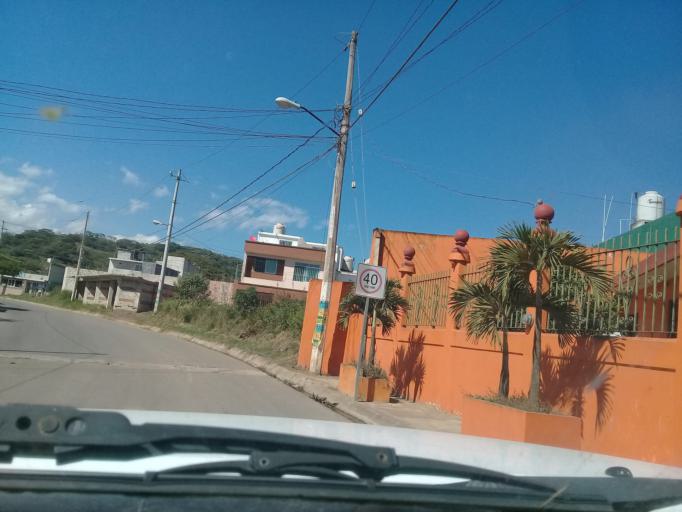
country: MX
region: Veracruz
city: El Castillo
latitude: 19.5517
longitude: -96.8542
